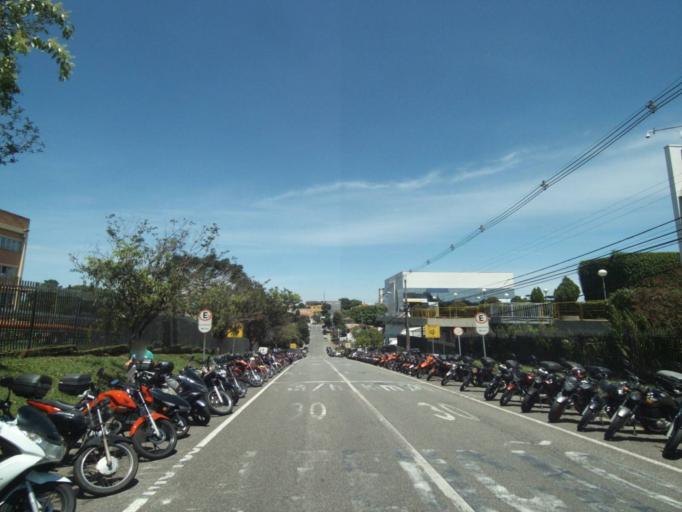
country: BR
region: Parana
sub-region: Pinhais
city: Pinhais
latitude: -25.4674
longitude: -49.2379
